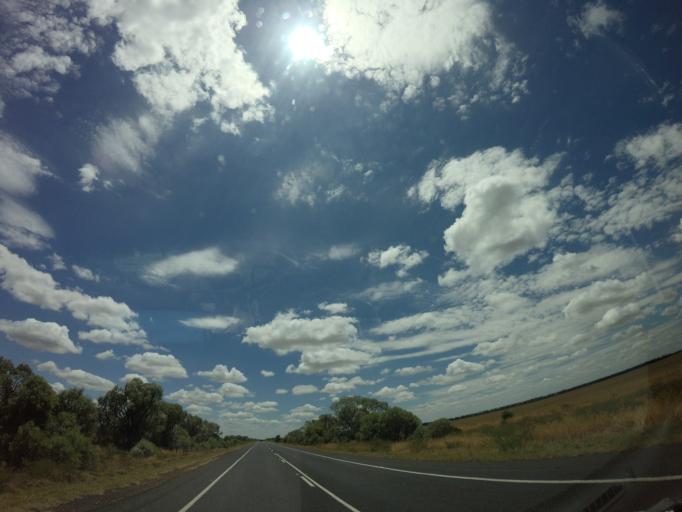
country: AU
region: New South Wales
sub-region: Moree Plains
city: Boggabilla
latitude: -28.8829
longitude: 150.1579
